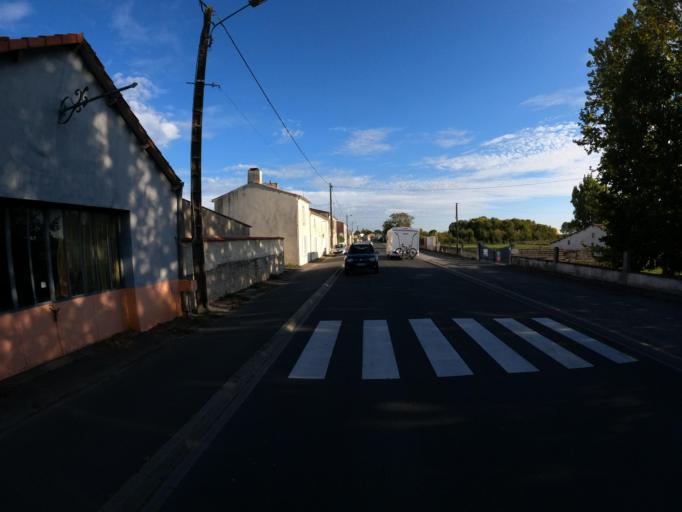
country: FR
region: Pays de la Loire
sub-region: Departement de la Vendee
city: Chaille-les-Marais
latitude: 46.3689
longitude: -0.9942
